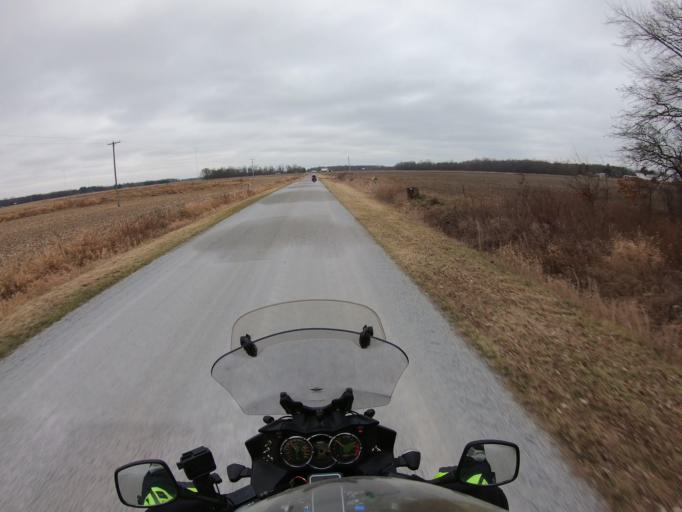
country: US
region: Michigan
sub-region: Saginaw County
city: Saint Charles
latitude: 43.2589
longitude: -84.0904
